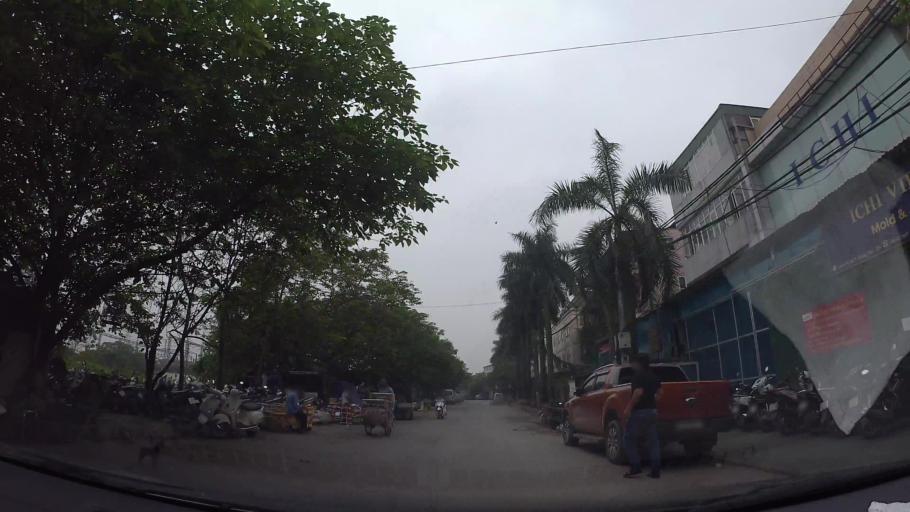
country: VN
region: Ha Noi
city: Hai BaTrung
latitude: 20.9826
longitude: 105.8682
